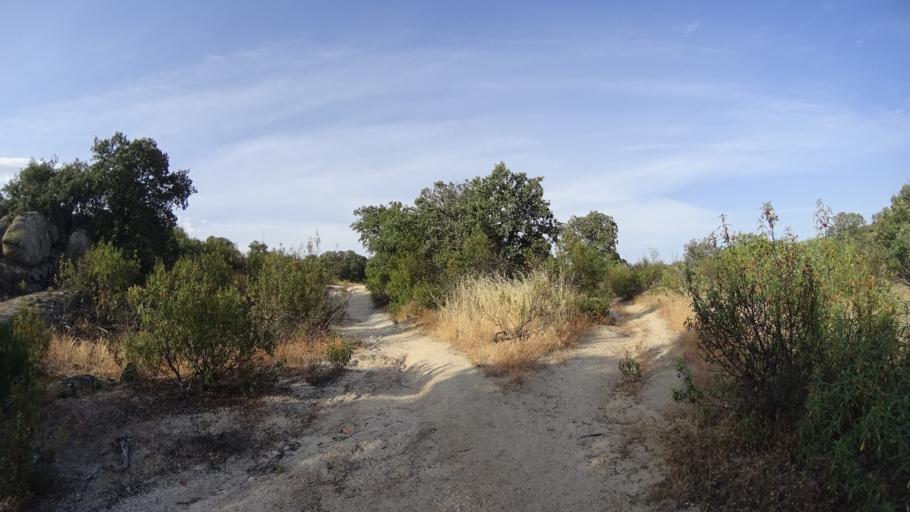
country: ES
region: Madrid
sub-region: Provincia de Madrid
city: Torrelodones
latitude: 40.5901
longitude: -3.9426
